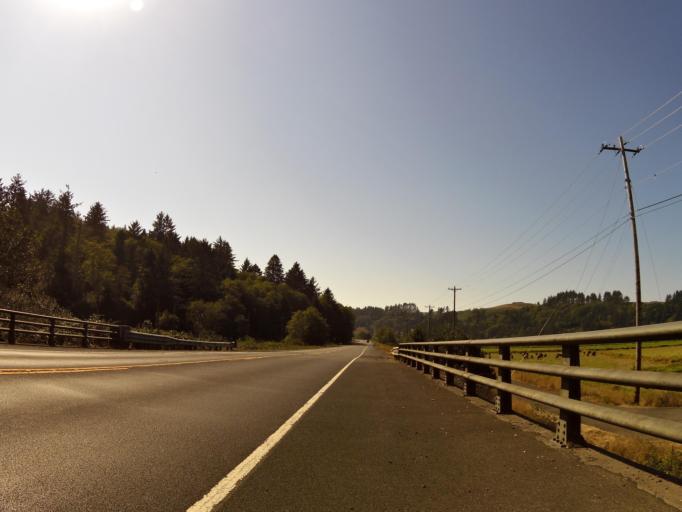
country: US
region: Oregon
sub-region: Tillamook County
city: Pacific City
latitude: 45.1610
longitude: -123.9384
